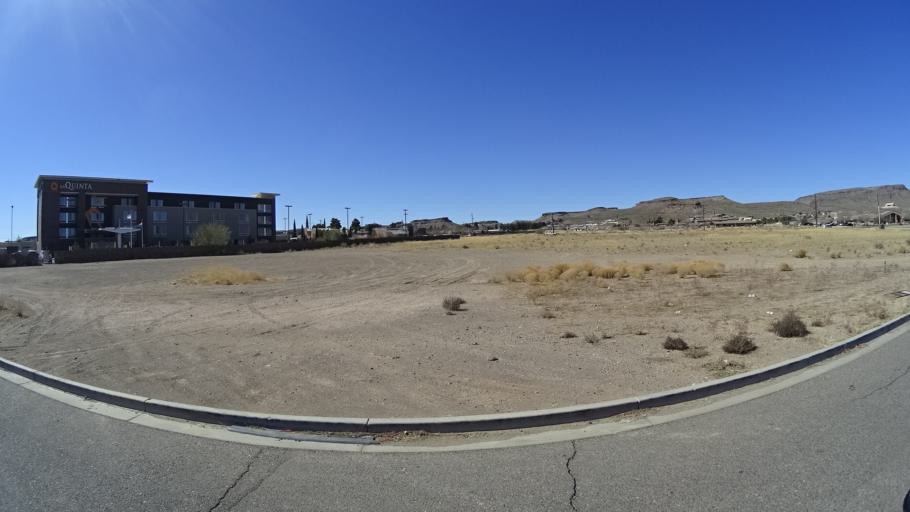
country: US
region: Arizona
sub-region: Mohave County
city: Kingman
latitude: 35.2241
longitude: -114.0381
